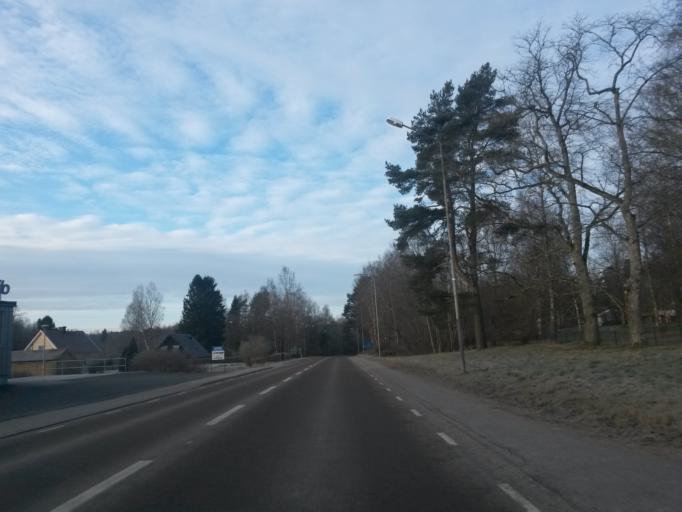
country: SE
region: Vaestra Goetaland
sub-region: Boras Kommun
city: Boras
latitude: 57.8263
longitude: 13.0023
